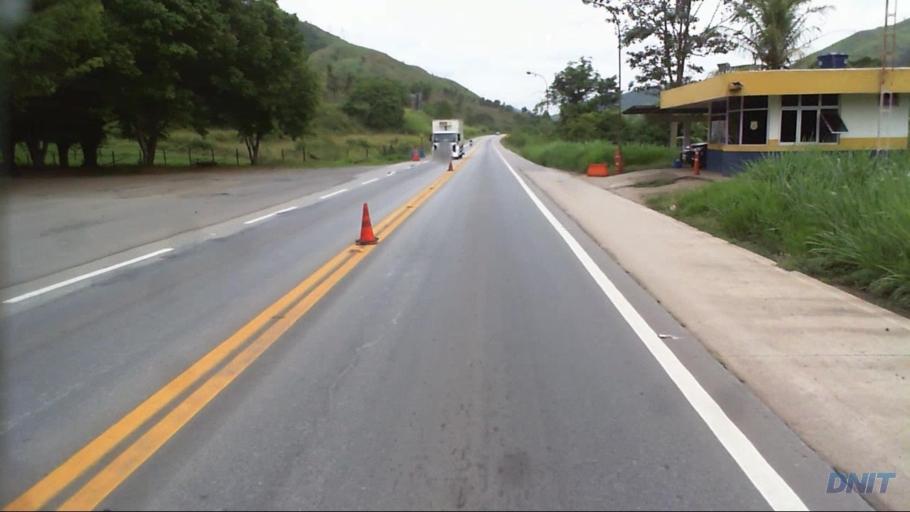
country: BR
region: Minas Gerais
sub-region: Timoteo
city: Timoteo
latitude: -19.5965
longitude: -42.7451
